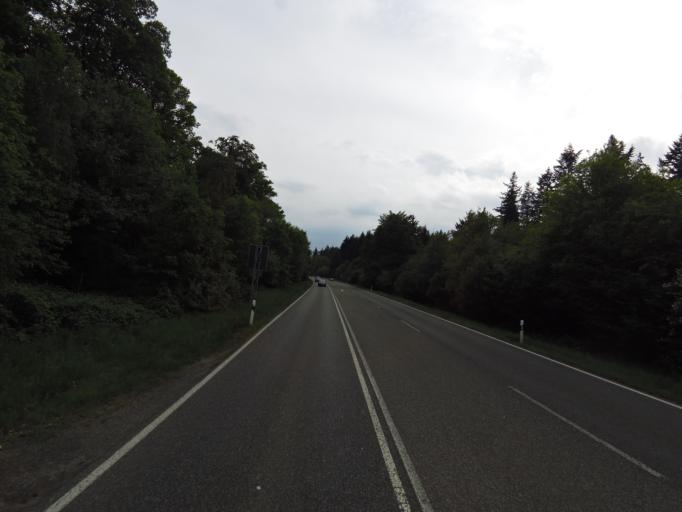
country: DE
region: Rheinland-Pfalz
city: Waldesch
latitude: 50.2608
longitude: 7.5279
